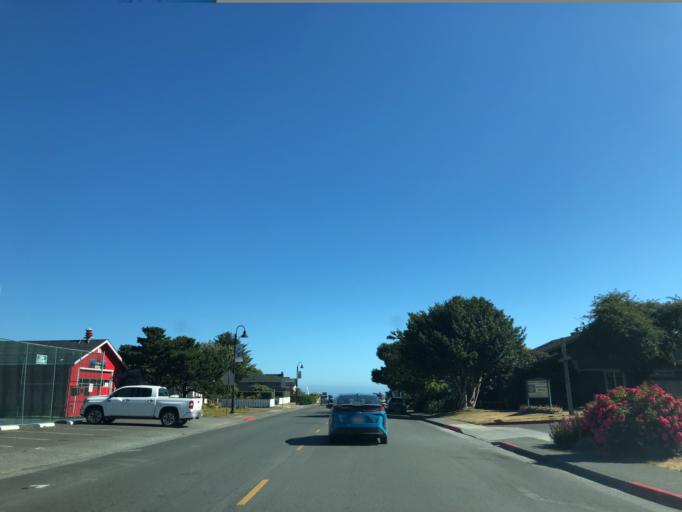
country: US
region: California
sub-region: Humboldt County
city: Westhaven-Moonstone
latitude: 41.0603
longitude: -124.1431
